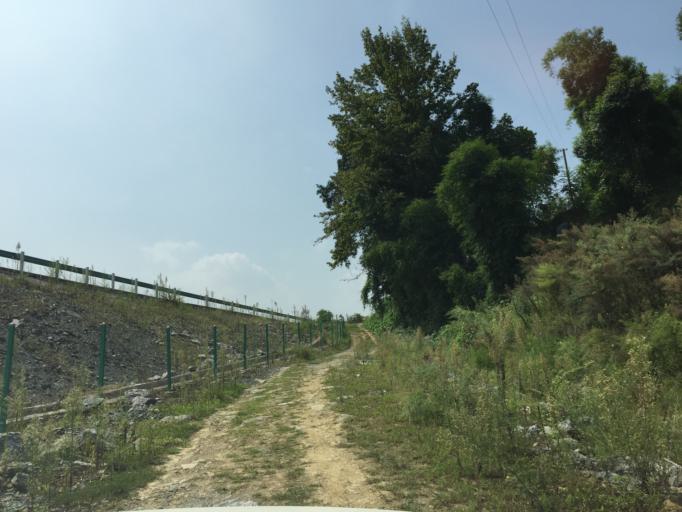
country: CN
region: Guizhou Sheng
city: Qinglong
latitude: 28.2953
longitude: 108.1118
